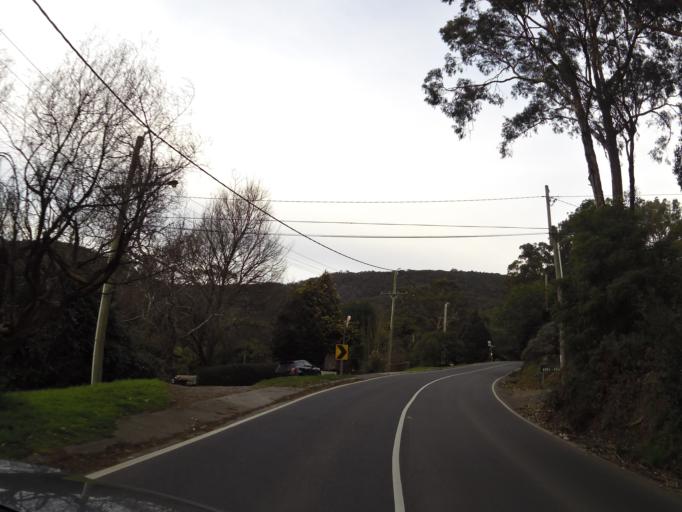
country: AU
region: Victoria
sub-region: Knox
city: The Basin
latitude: -37.8608
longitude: 145.3214
